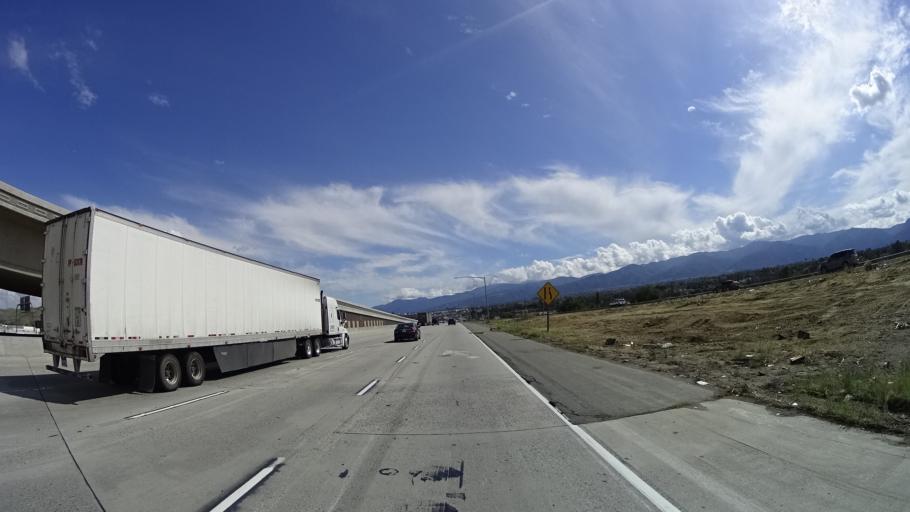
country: US
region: California
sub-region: Riverside County
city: Corona
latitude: 33.8784
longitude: -117.5464
